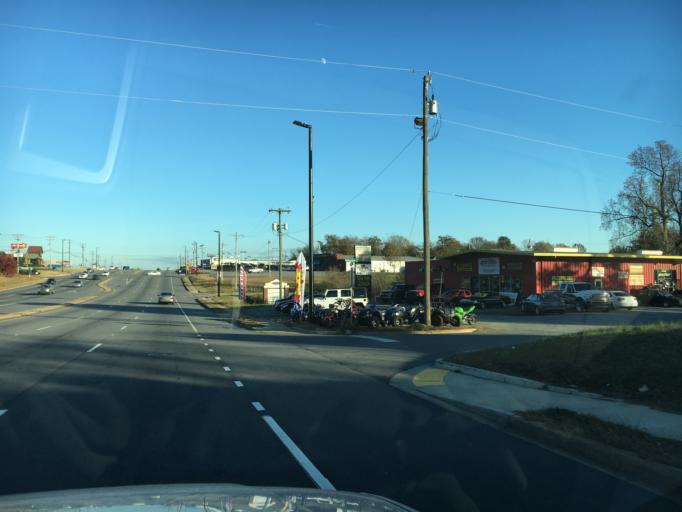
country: US
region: South Carolina
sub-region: Greenville County
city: Greer
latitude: 34.9479
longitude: -82.2215
